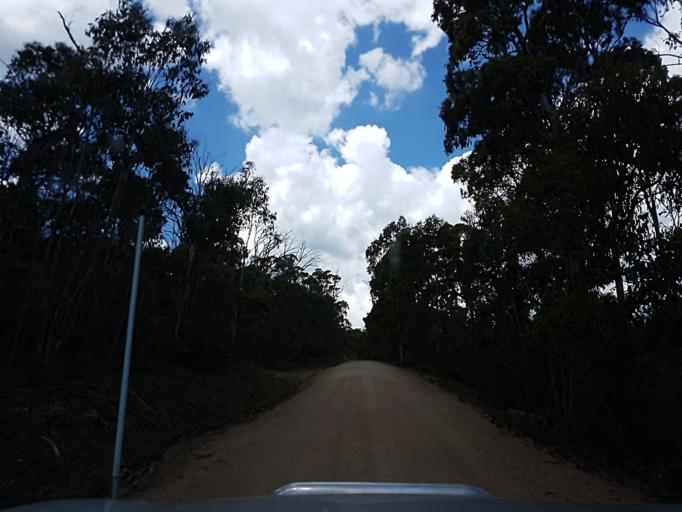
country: AU
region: New South Wales
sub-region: Snowy River
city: Jindabyne
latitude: -36.9117
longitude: 148.1205
